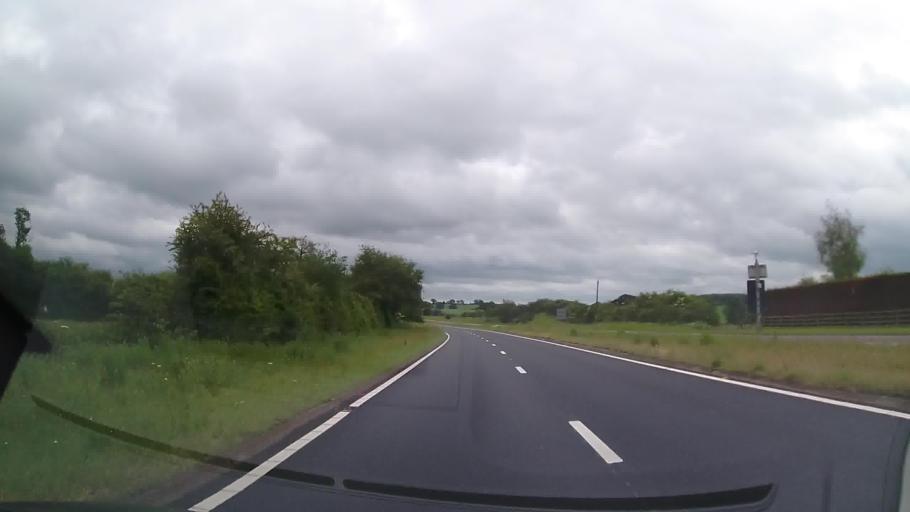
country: GB
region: England
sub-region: Shropshire
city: Stoke upon Tern
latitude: 52.9032
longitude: -2.5739
